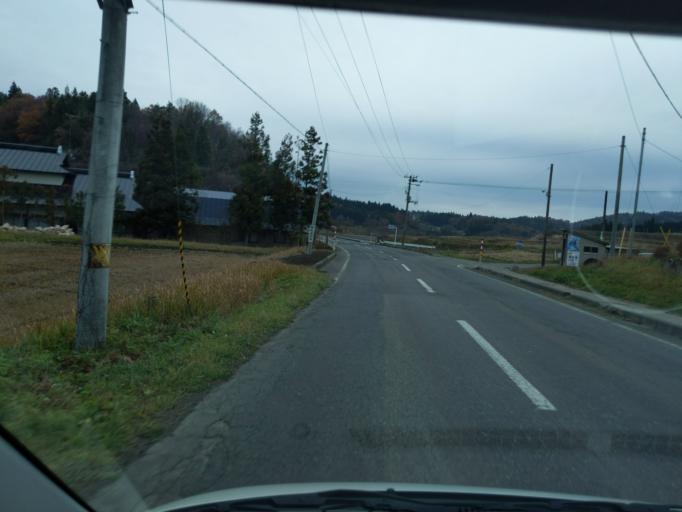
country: JP
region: Iwate
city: Kitakami
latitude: 39.2698
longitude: 141.2676
